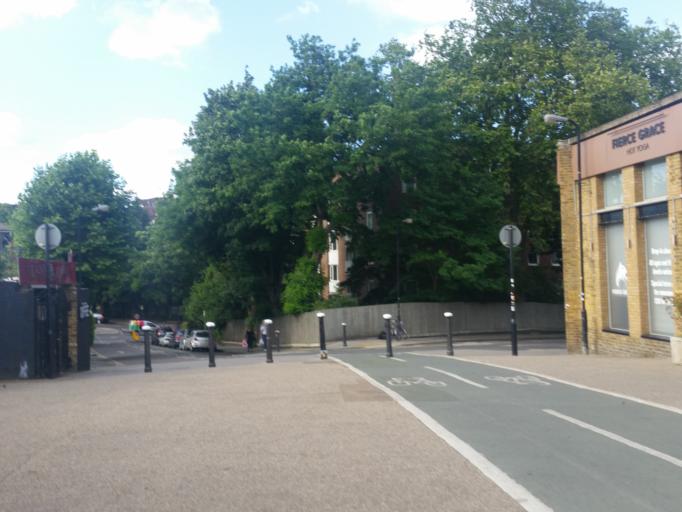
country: GB
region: England
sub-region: Greater London
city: Camden Town
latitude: 51.5430
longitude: -0.1550
